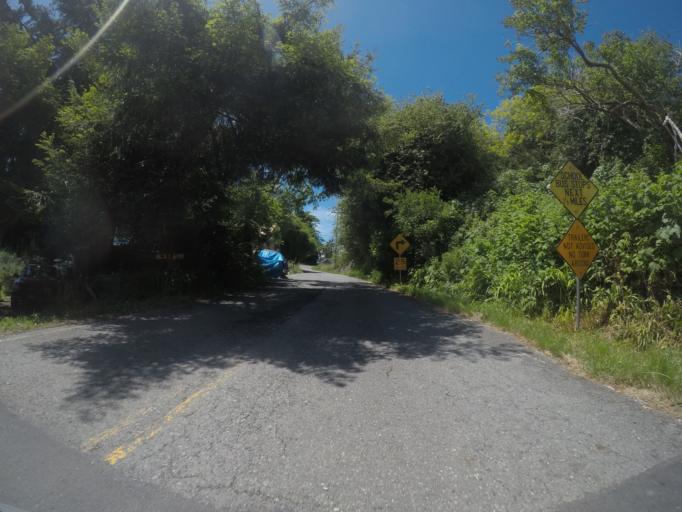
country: US
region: California
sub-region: Del Norte County
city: Bertsch-Oceanview
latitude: 41.5469
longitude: -124.0653
